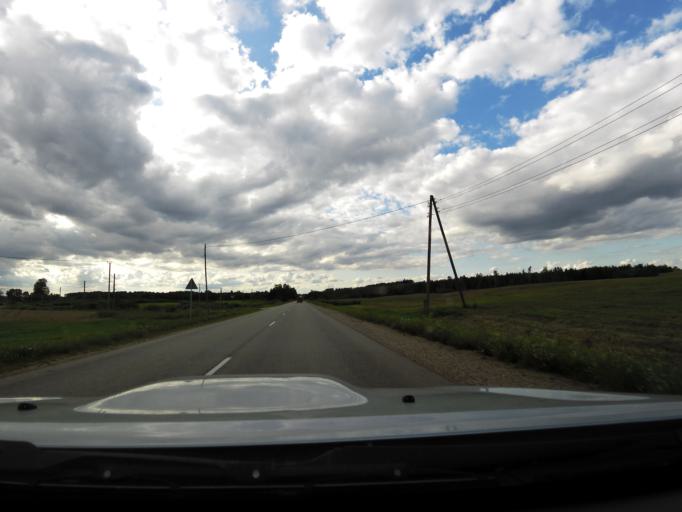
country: LV
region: Ilukste
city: Ilukste
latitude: 55.9647
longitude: 26.0448
